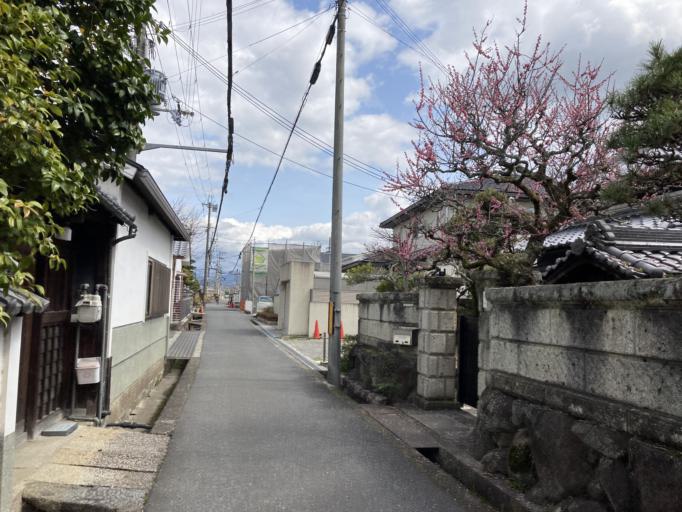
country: JP
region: Nara
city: Kashihara-shi
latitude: 34.5029
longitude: 135.7987
